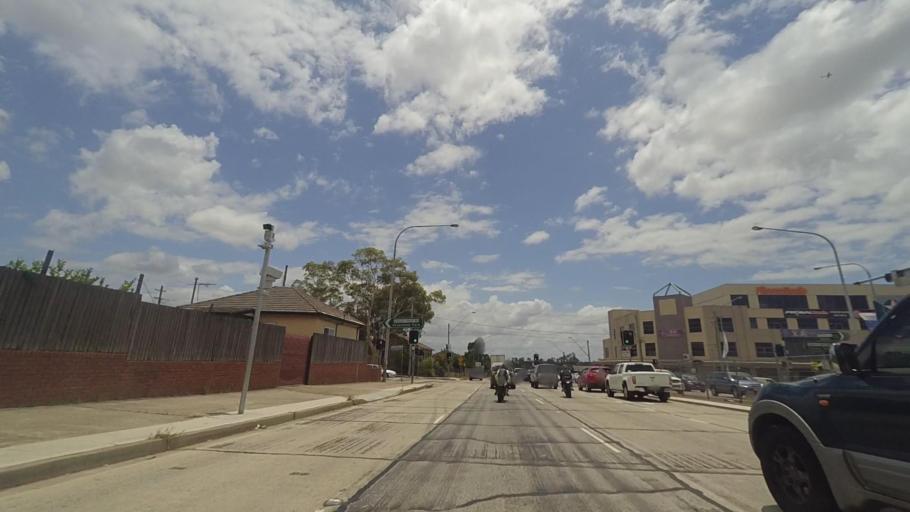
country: AU
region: New South Wales
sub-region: Fairfield
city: Cabramatta West
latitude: -33.8841
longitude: 150.9237
